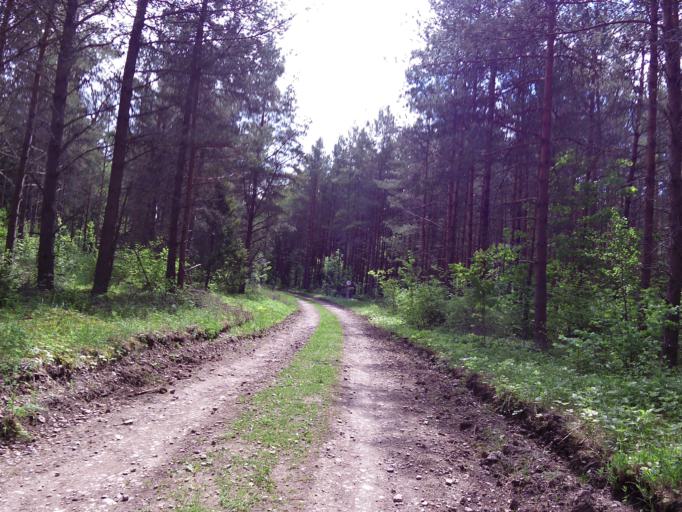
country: EE
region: Harju
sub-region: Paldiski linn
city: Paldiski
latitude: 59.2603
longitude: 23.7454
